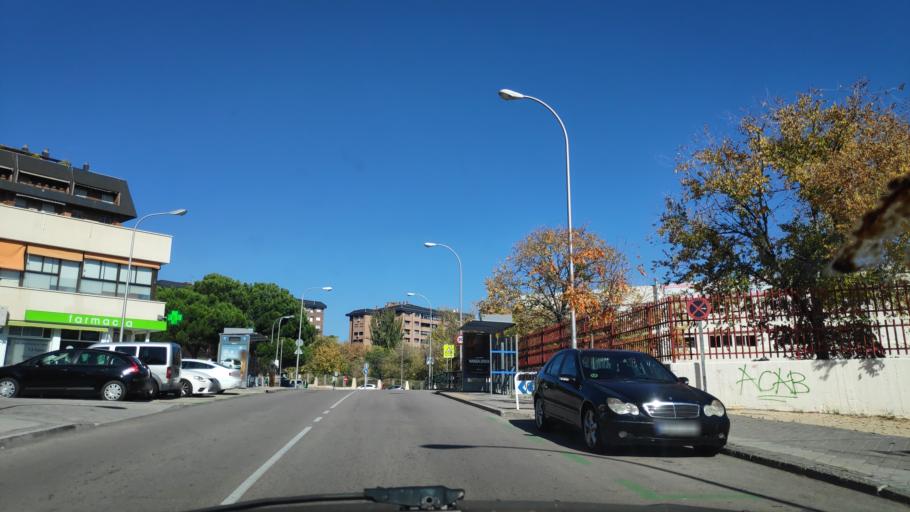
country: ES
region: Madrid
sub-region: Provincia de Madrid
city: Tetuan de las Victorias
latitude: 40.4867
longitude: -3.7016
